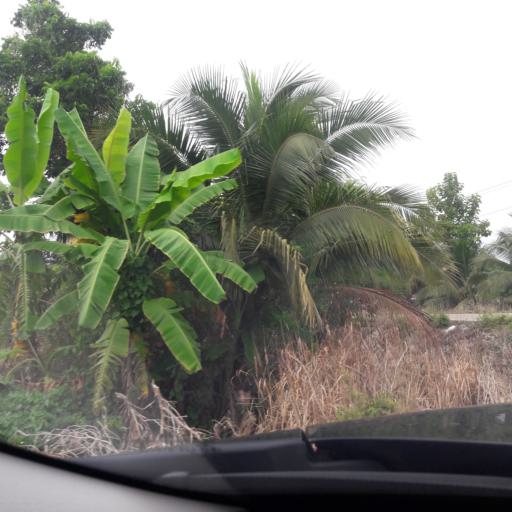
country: TH
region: Ratchaburi
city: Damnoen Saduak
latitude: 13.5727
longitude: 99.9409
